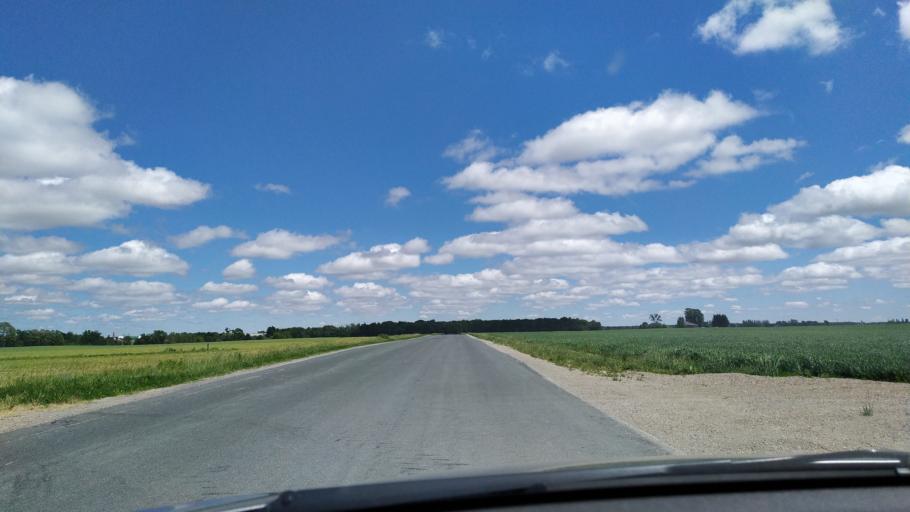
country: CA
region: Ontario
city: Huron East
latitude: 43.4545
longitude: -81.1913
